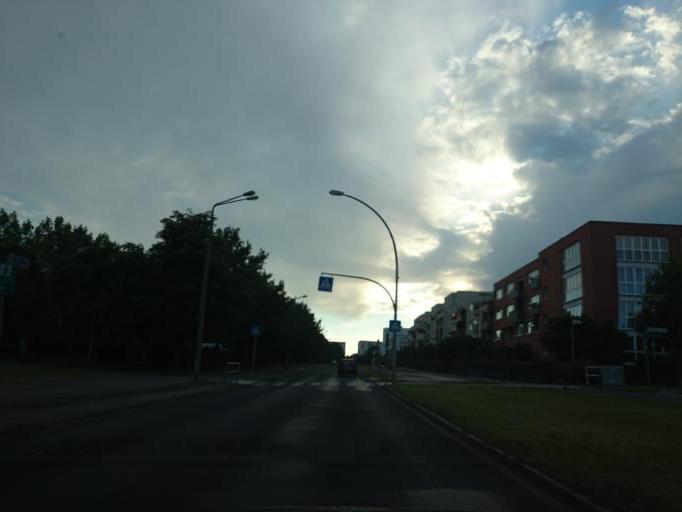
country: DE
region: Berlin
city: Marzahn
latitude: 52.5401
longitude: 13.5770
